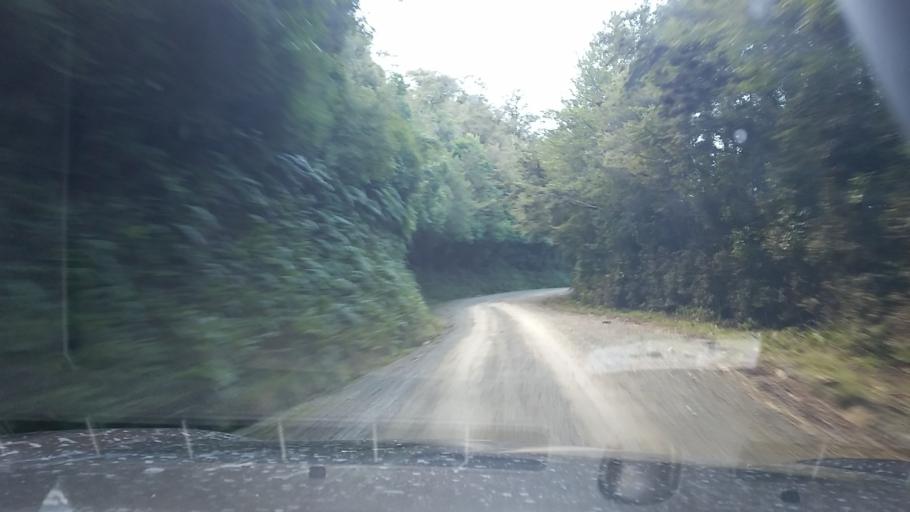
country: NZ
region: Marlborough
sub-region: Marlborough District
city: Picton
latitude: -41.0953
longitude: 174.1352
